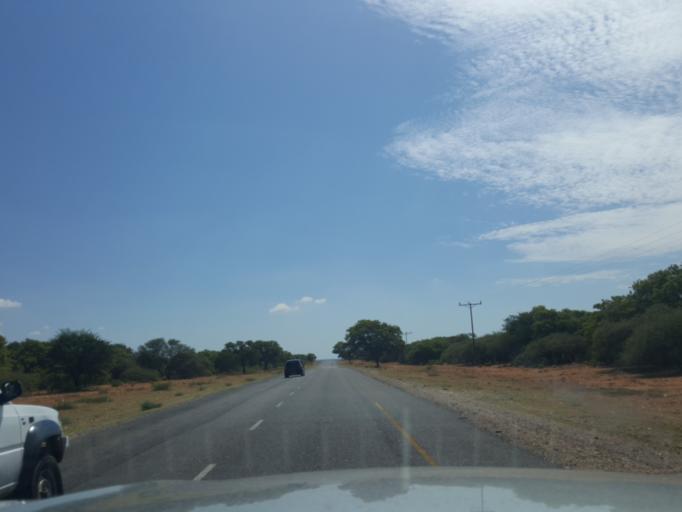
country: BW
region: Kweneng
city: Letlhakeng
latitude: -24.1232
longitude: 25.0935
